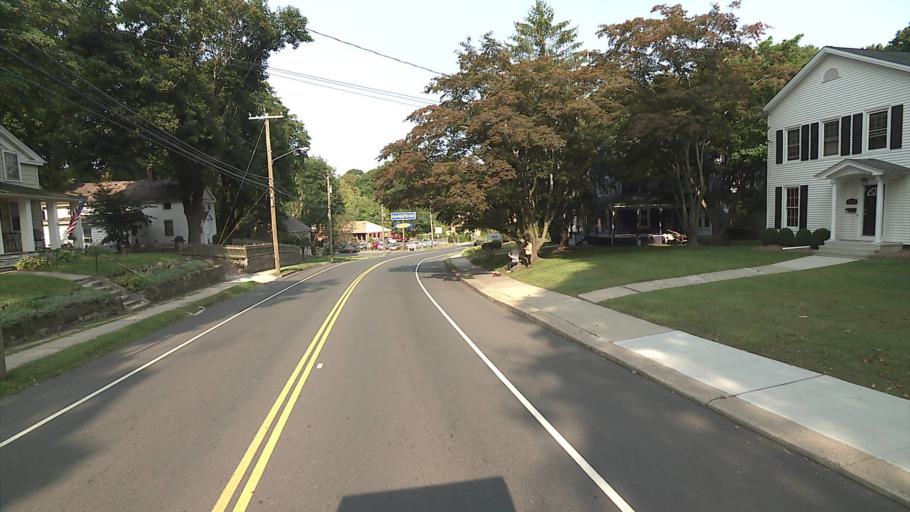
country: US
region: Connecticut
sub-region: Fairfield County
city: Bethel
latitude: 41.3724
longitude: -73.4205
